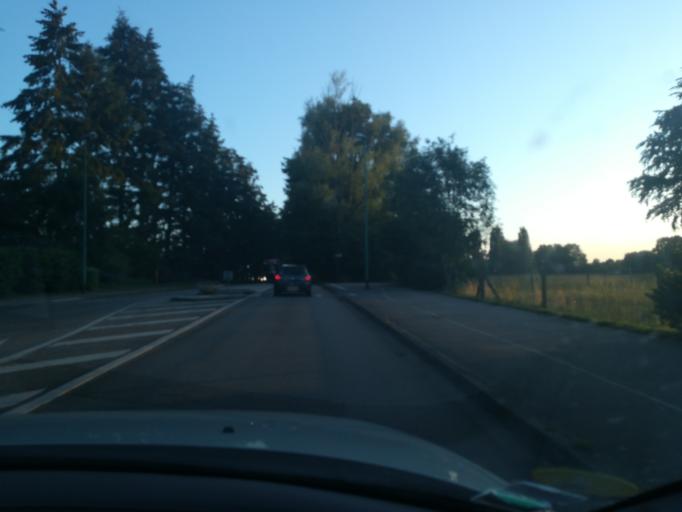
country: FR
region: Haute-Normandie
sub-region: Departement de la Seine-Maritime
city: Bois-Guillaume
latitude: 49.4661
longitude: 1.1321
